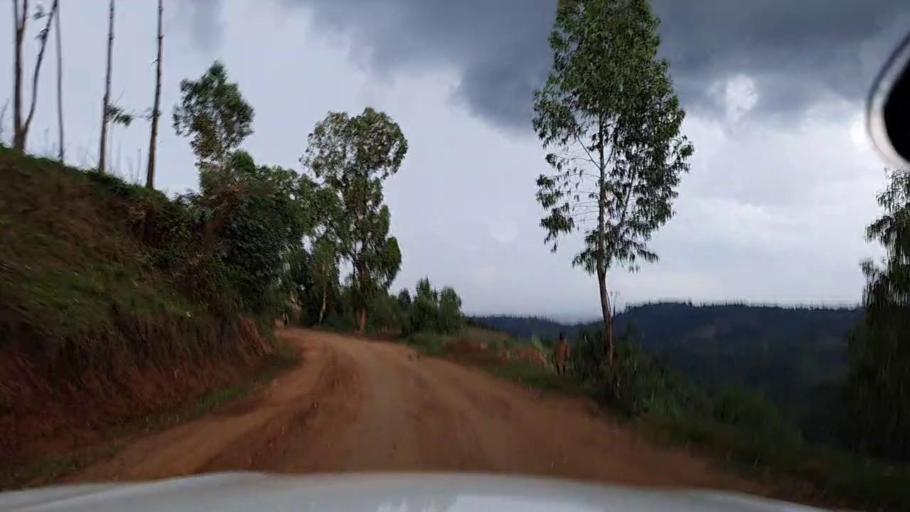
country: BI
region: Kayanza
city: Kayanza
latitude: -2.7890
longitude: 29.5276
